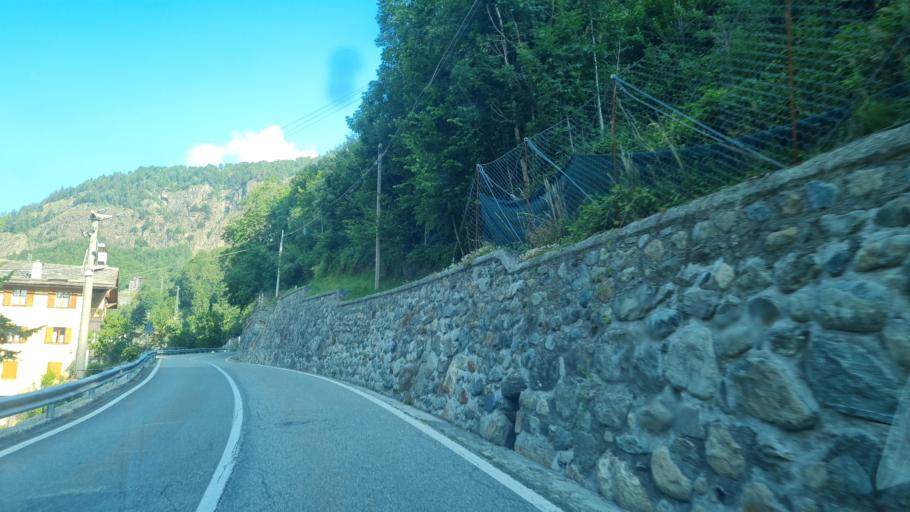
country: IT
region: Aosta Valley
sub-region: Valle d'Aosta
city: Pont-Bozet
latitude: 45.6194
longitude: 7.6666
